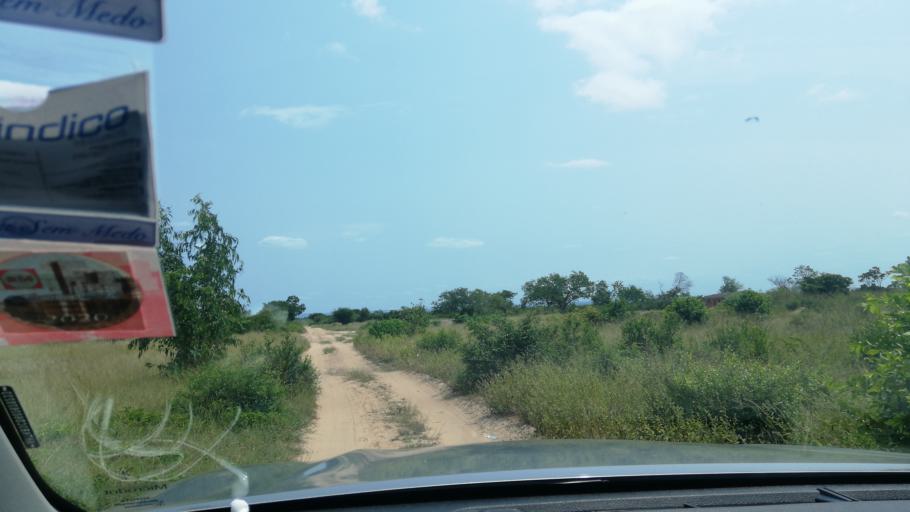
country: MZ
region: Maputo
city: Matola
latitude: -26.1101
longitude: 32.4141
